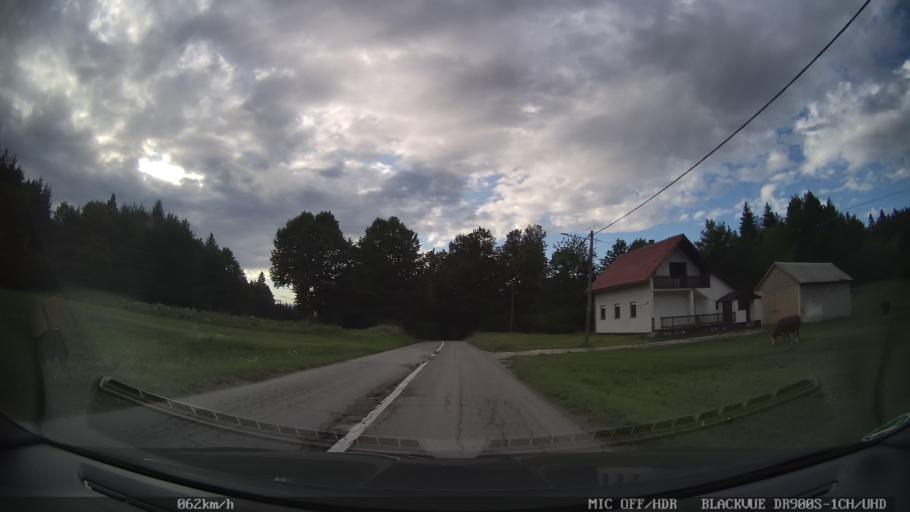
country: HR
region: Licko-Senjska
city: Jezerce
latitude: 44.9660
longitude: 15.5203
